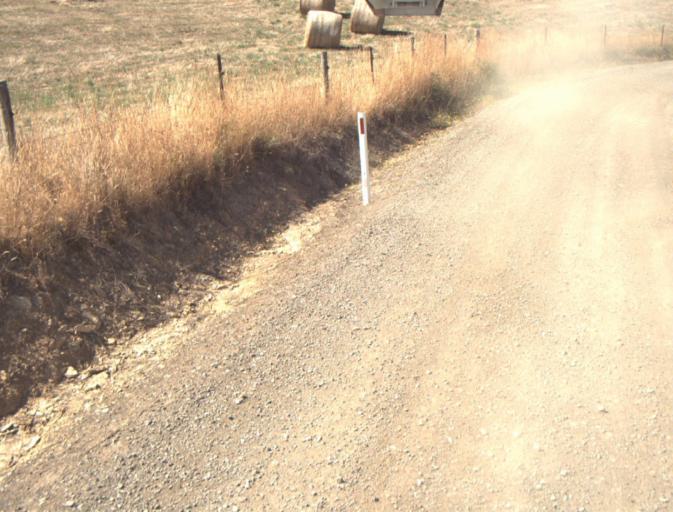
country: AU
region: Tasmania
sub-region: Launceston
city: Mayfield
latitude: -41.2227
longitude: 147.2387
